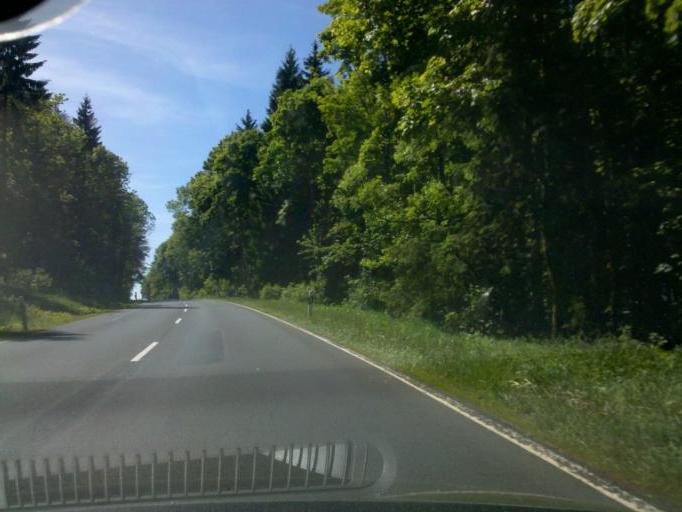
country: DE
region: Rheinland-Pfalz
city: Rehe
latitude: 50.6521
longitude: 8.1196
